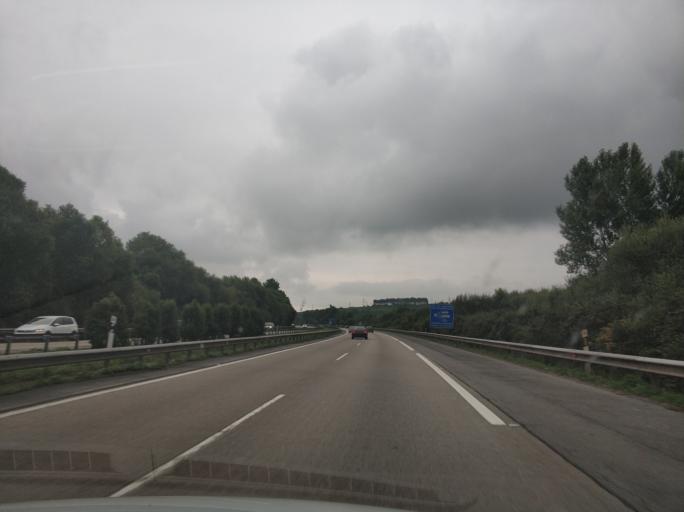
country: ES
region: Asturias
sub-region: Province of Asturias
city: Corvera de Asturias
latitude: 43.5213
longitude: -5.8228
